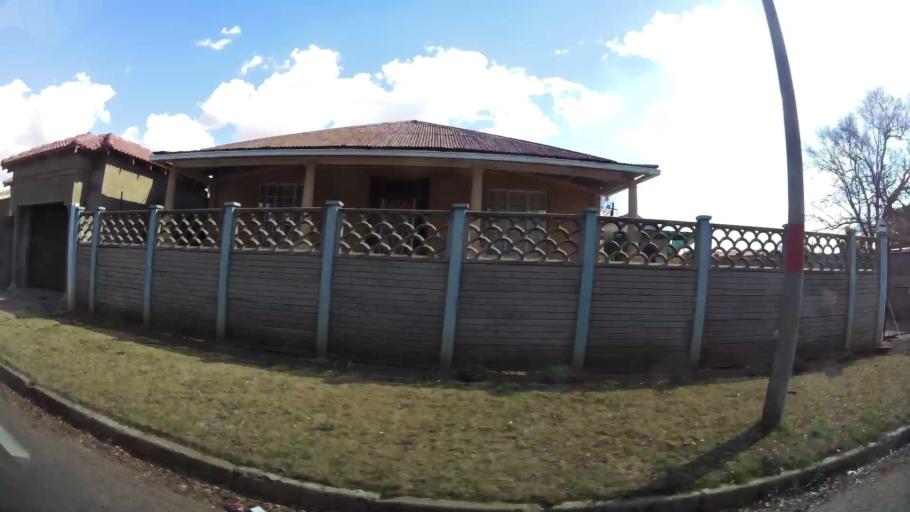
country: ZA
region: North-West
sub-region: Dr Kenneth Kaunda District Municipality
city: Klerksdorp
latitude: -26.8569
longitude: 26.6544
